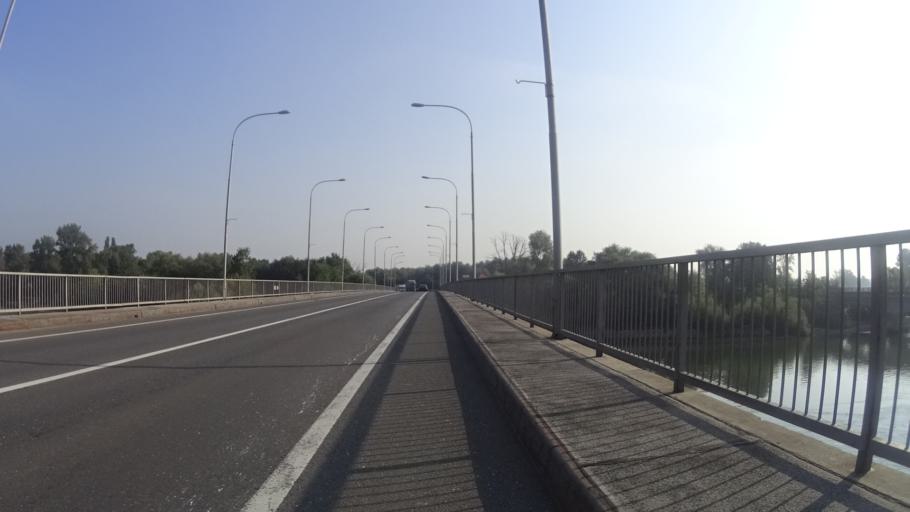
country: HR
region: Varazdinska
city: Varazdin
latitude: 46.3218
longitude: 16.3579
